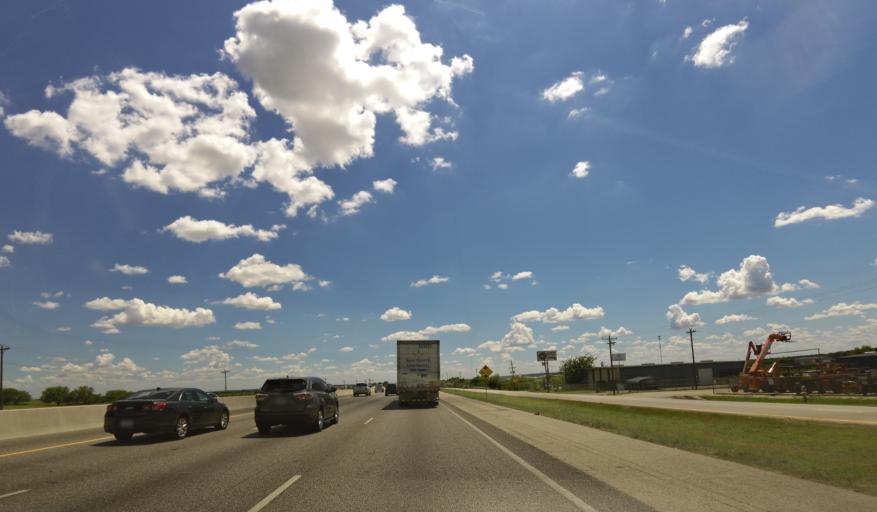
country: US
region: Texas
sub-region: Hays County
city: San Marcos
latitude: 29.8211
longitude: -97.9931
